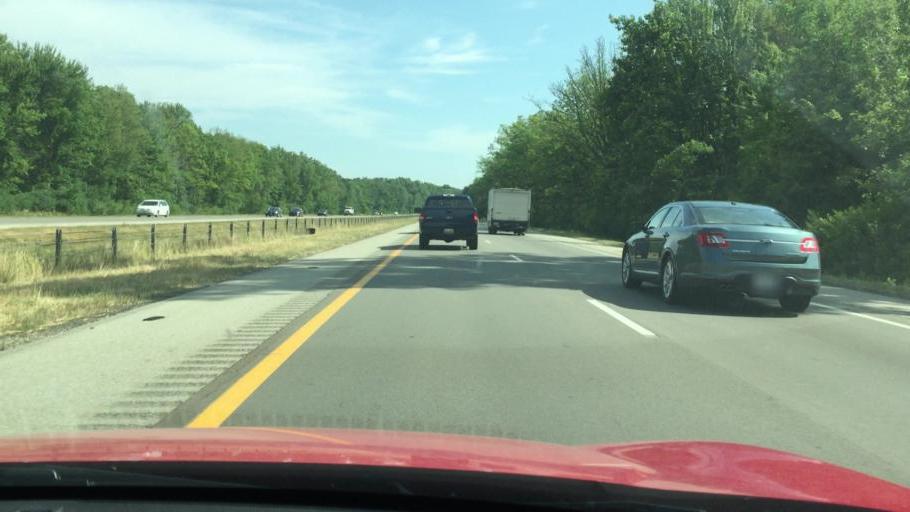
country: US
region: Michigan
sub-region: Washtenaw County
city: Milan
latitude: 42.0498
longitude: -83.6701
